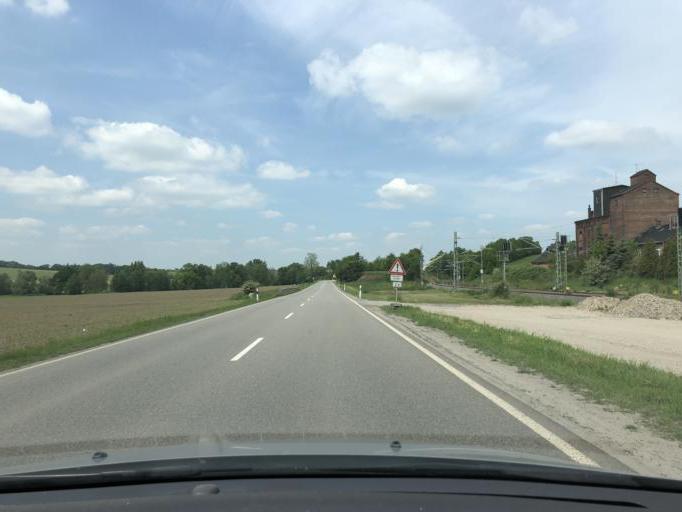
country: DE
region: Thuringia
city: Saara
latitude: 50.9391
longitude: 12.4249
